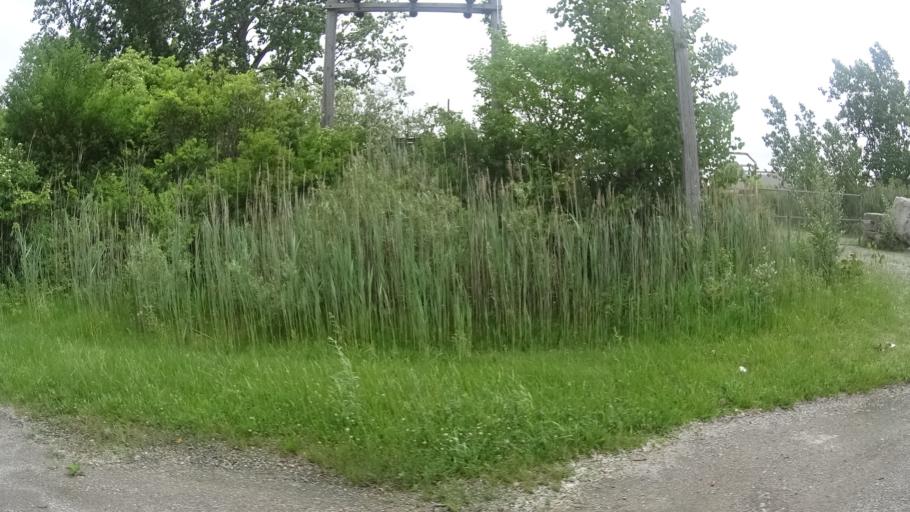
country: US
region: Ohio
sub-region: Huron County
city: Bellevue
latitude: 41.3376
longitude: -82.7937
